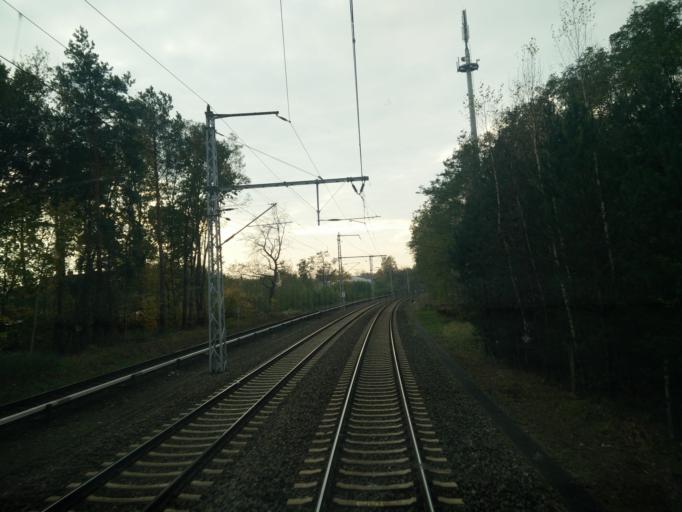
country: DE
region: Brandenburg
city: Wildau
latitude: 52.3331
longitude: 13.6372
